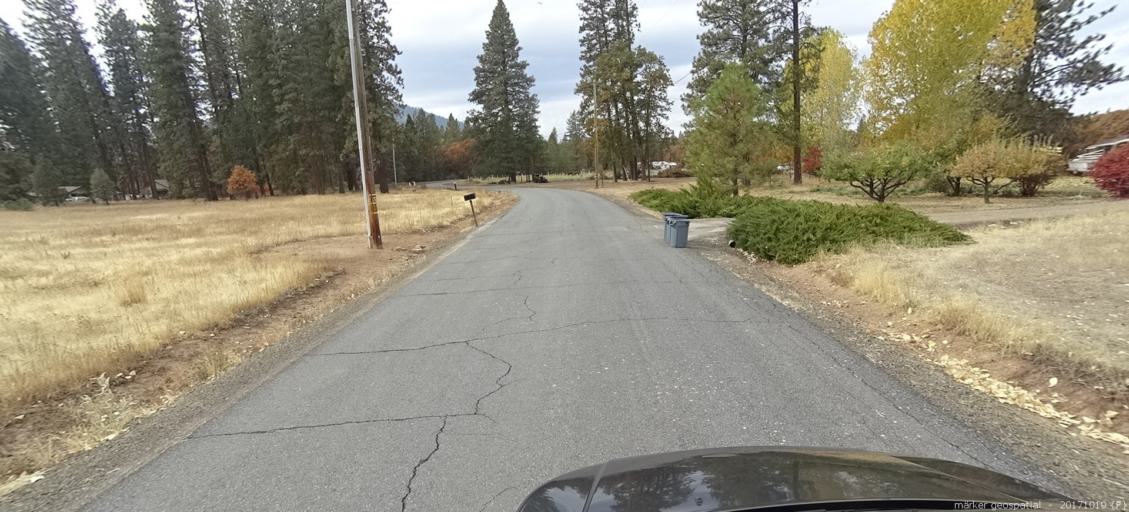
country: US
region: California
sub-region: Shasta County
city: Burney
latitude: 41.0891
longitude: -121.5188
